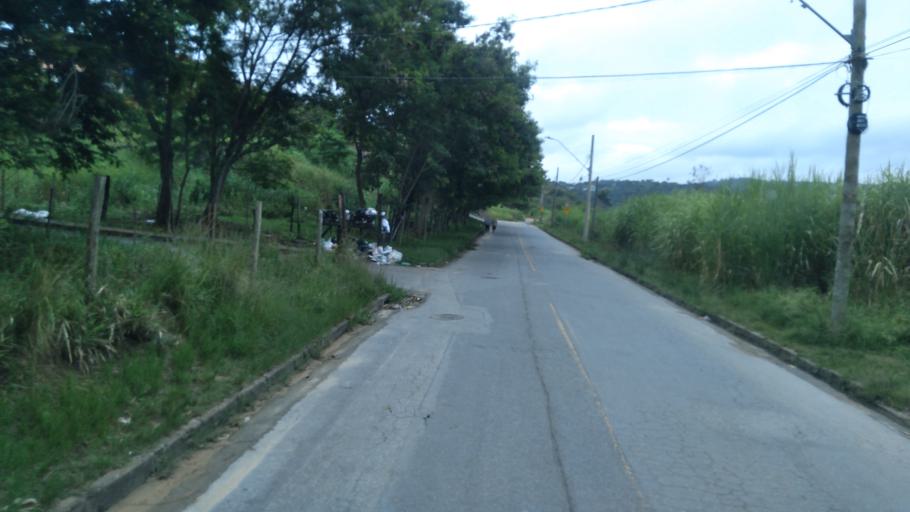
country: BR
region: Minas Gerais
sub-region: Santa Luzia
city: Santa Luzia
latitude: -19.8337
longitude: -43.8677
